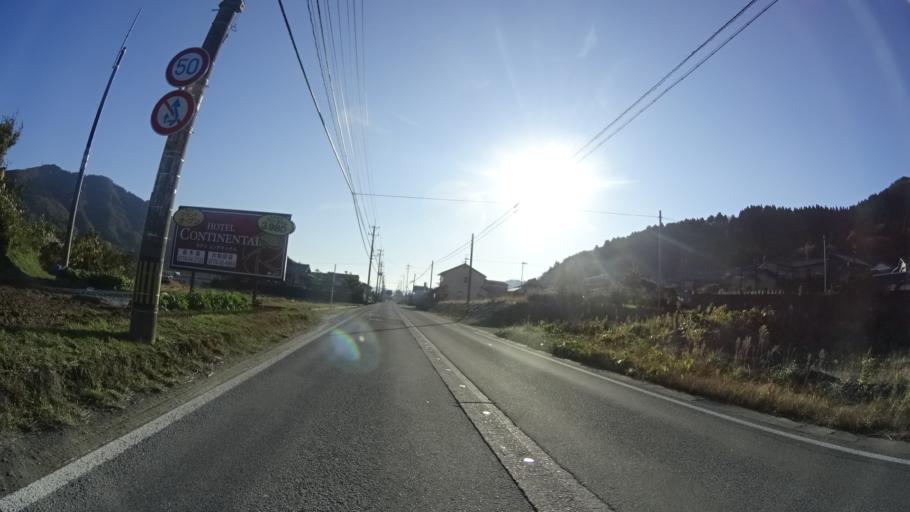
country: JP
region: Fukui
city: Maruoka
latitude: 36.1004
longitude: 136.3197
